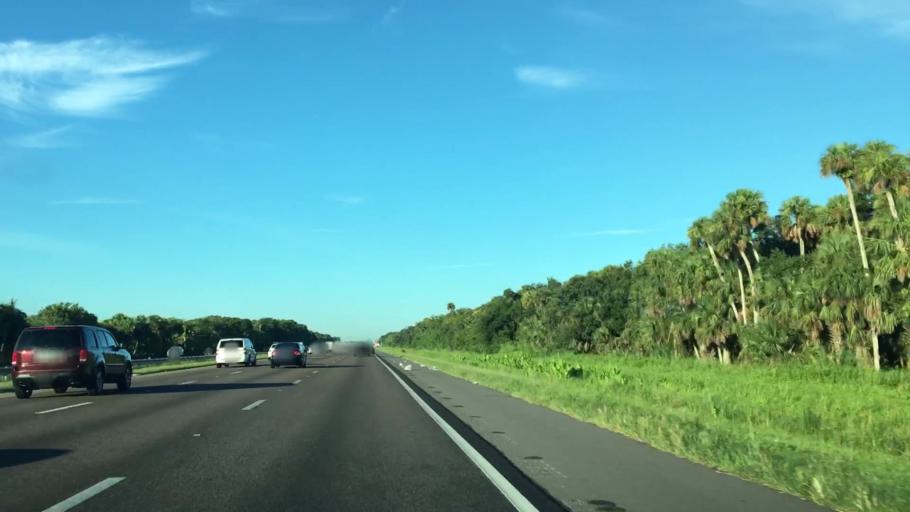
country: US
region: Florida
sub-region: Volusia County
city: DeBary
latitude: 28.8513
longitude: -81.3045
